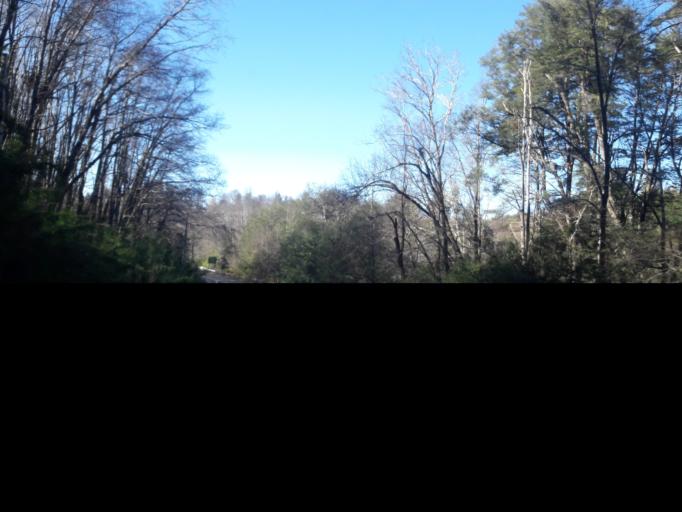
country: CL
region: Araucania
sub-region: Provincia de Malleco
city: Victoria
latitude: -38.3319
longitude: -71.9753
